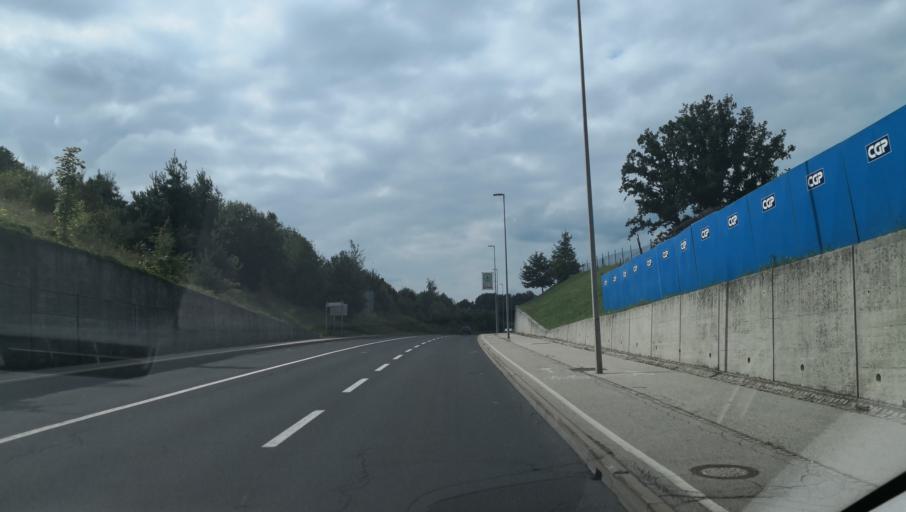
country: SI
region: Novo Mesto
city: Novo Mesto
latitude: 45.8157
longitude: 15.1749
